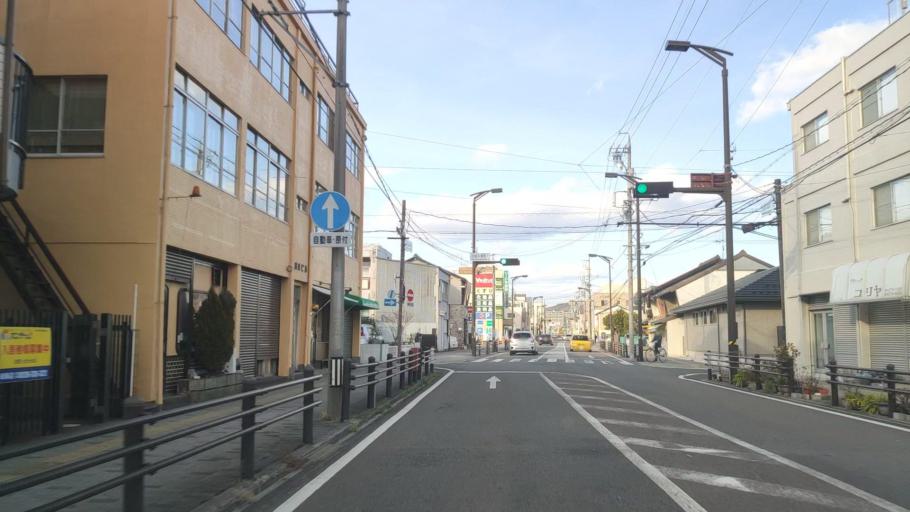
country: JP
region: Gifu
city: Gifu-shi
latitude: 35.4002
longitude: 136.7570
